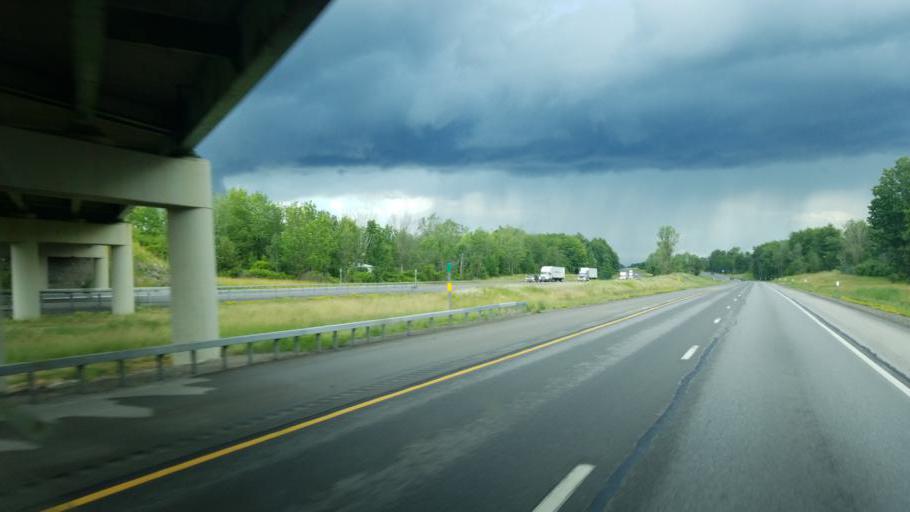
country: US
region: New York
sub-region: Erie County
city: Angola
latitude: 42.6011
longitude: -79.0323
